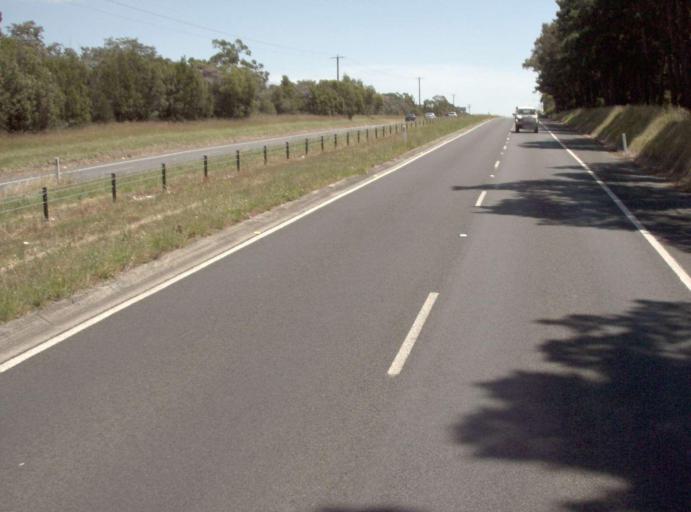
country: AU
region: Victoria
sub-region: Latrobe
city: Traralgon
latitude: -38.2058
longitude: 146.5080
